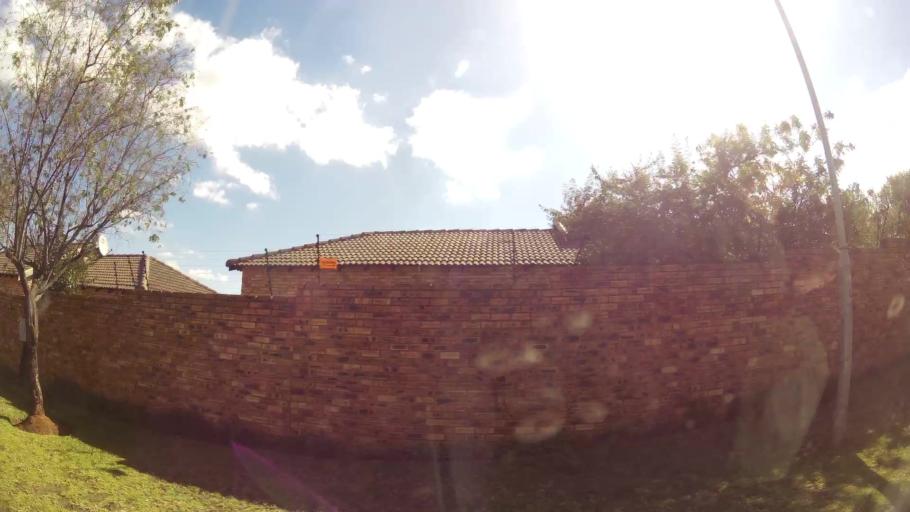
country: ZA
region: Gauteng
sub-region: City of Johannesburg Metropolitan Municipality
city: Midrand
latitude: -25.9947
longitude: 28.1008
